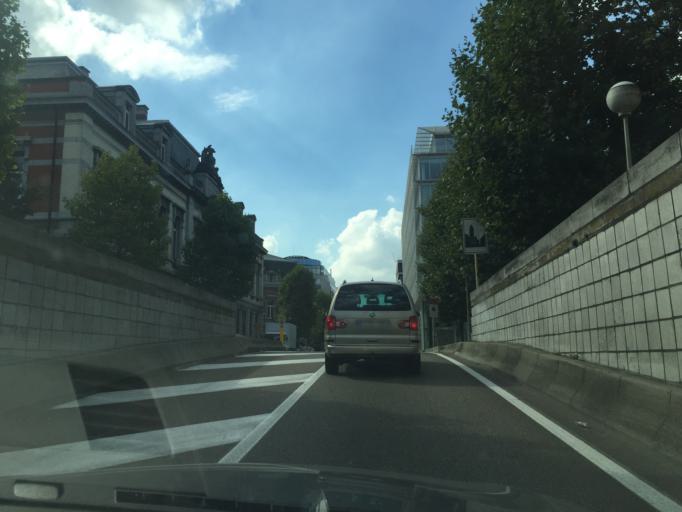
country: BE
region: Brussels Capital
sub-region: Bruxelles-Capitale
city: Brussels
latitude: 50.8464
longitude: 4.3928
